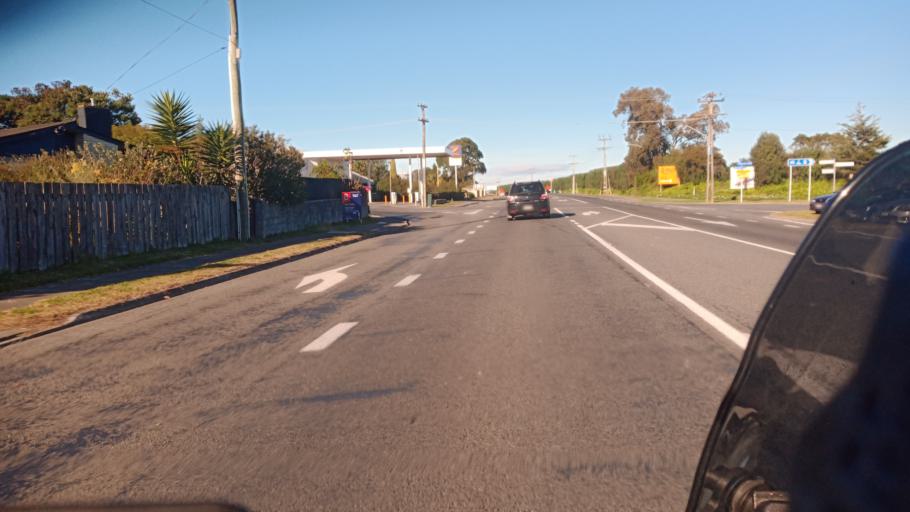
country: NZ
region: Hawke's Bay
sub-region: Napier City
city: Napier
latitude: -39.4364
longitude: 176.8702
